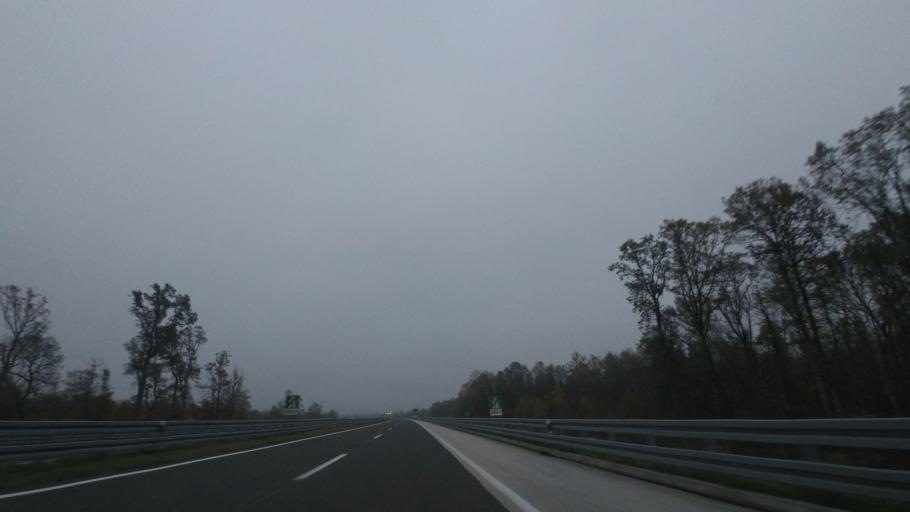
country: HR
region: Sisacko-Moslavacka
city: Lekenik
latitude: 45.5740
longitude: 16.2045
